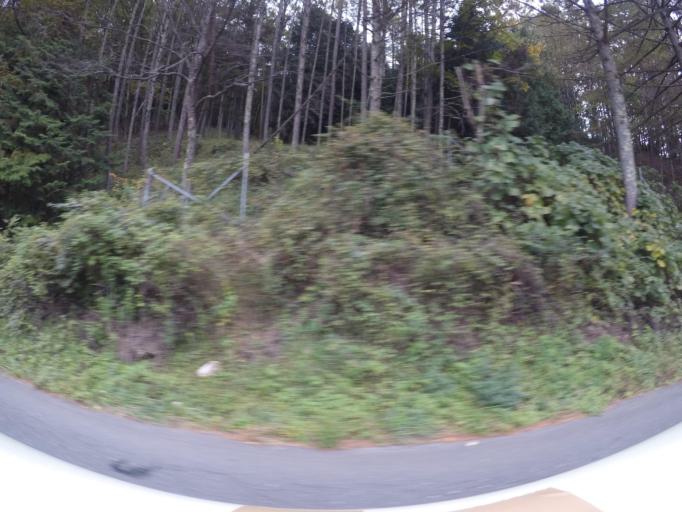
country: JP
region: Nagano
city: Chino
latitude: 35.9180
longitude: 138.0945
